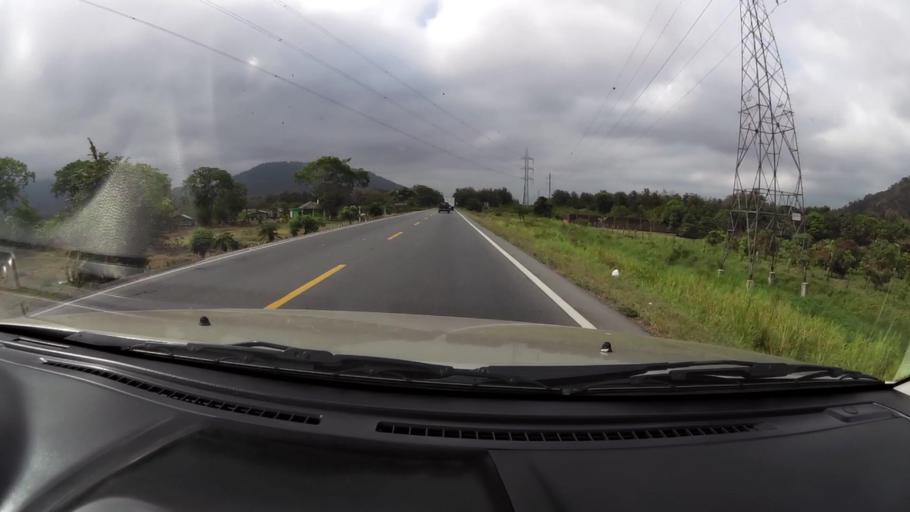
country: EC
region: Guayas
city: Naranjal
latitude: -2.4139
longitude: -79.6240
